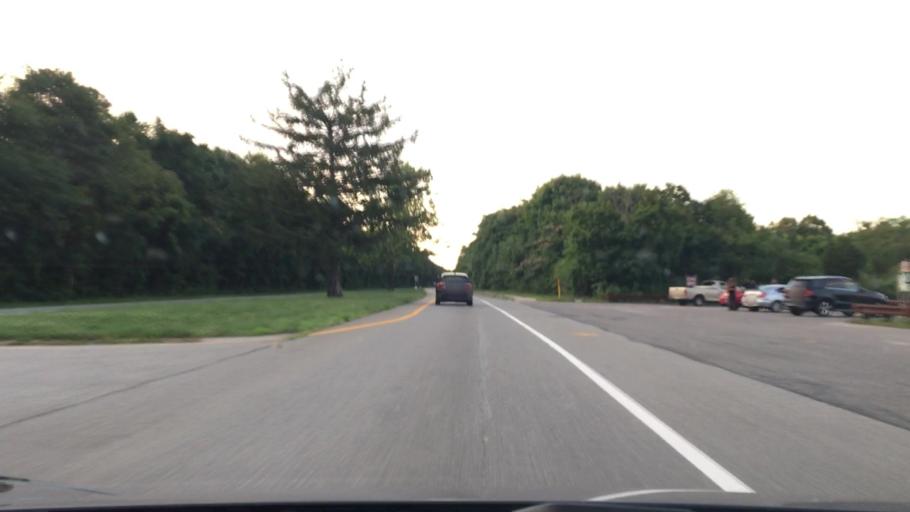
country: US
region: New York
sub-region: Suffolk County
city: Deer Park
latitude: 40.7765
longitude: -73.3104
